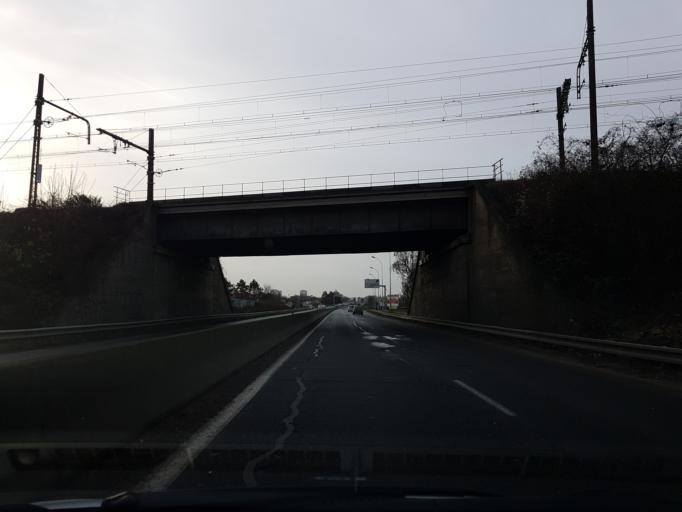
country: FR
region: Ile-de-France
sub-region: Departement de l'Essonne
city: Montgeron
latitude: 48.7147
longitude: 2.4424
